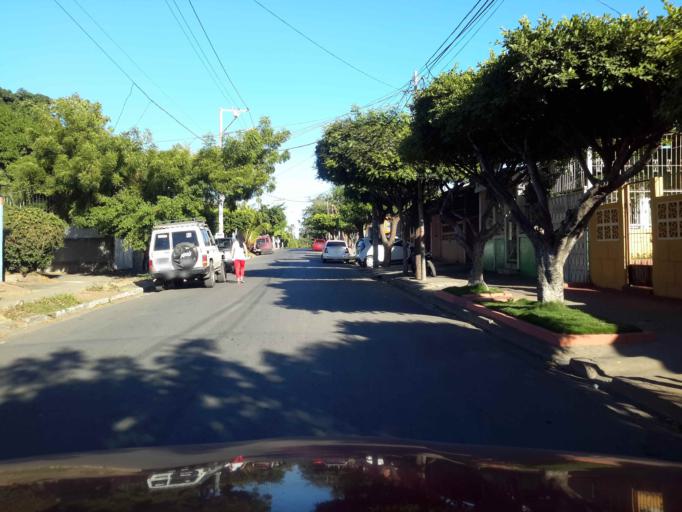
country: NI
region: Managua
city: Managua
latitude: 12.1122
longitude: -86.2929
